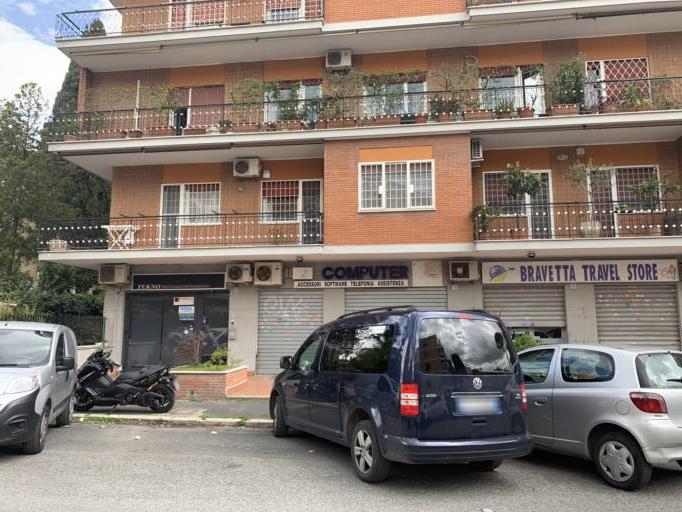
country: VA
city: Vatican City
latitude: 41.8816
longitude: 12.4264
